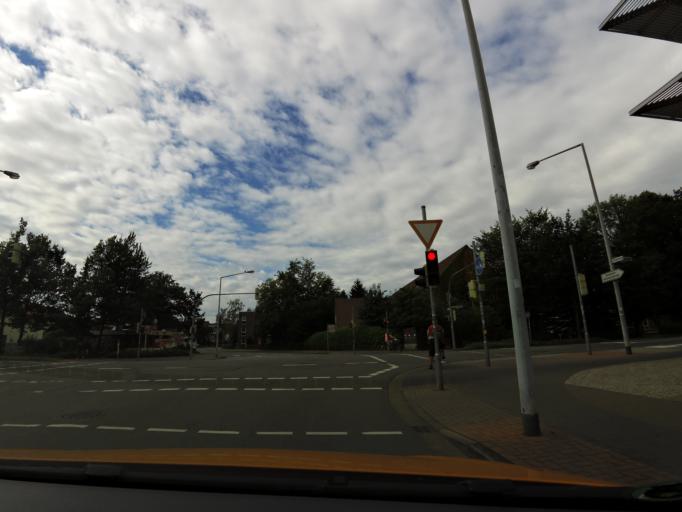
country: DE
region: Lower Saxony
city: Oldenburg
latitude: 53.1466
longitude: 8.1868
